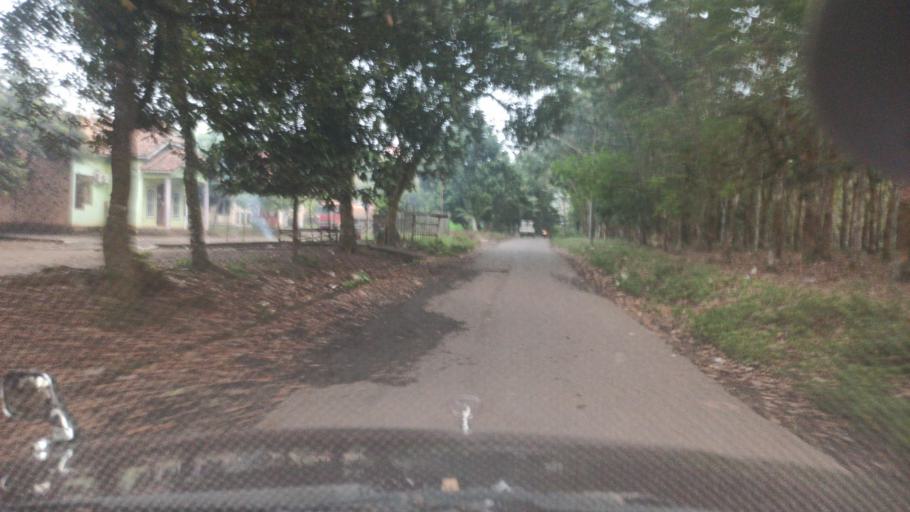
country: ID
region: South Sumatra
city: Gunungmenang
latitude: -3.2904
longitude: 104.1368
